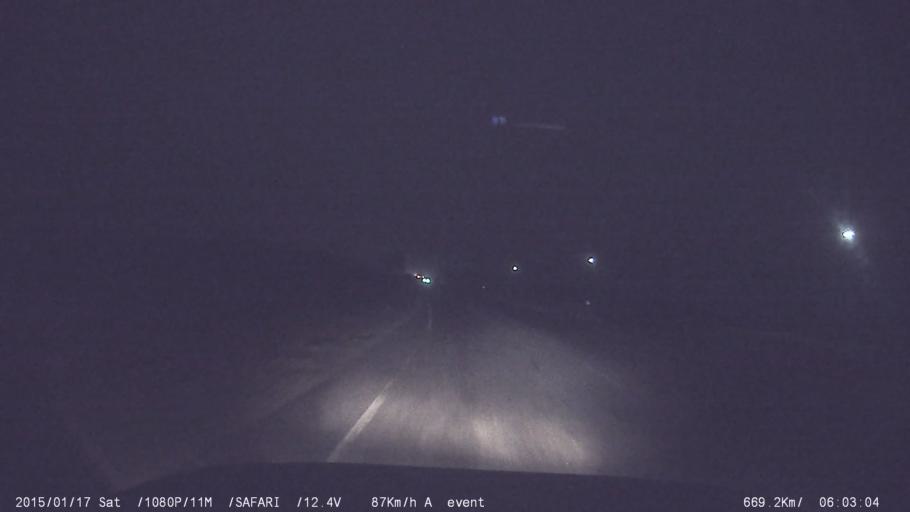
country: IN
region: Tamil Nadu
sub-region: Kancheepuram
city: Kanchipuram
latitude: 12.8837
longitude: 79.5985
